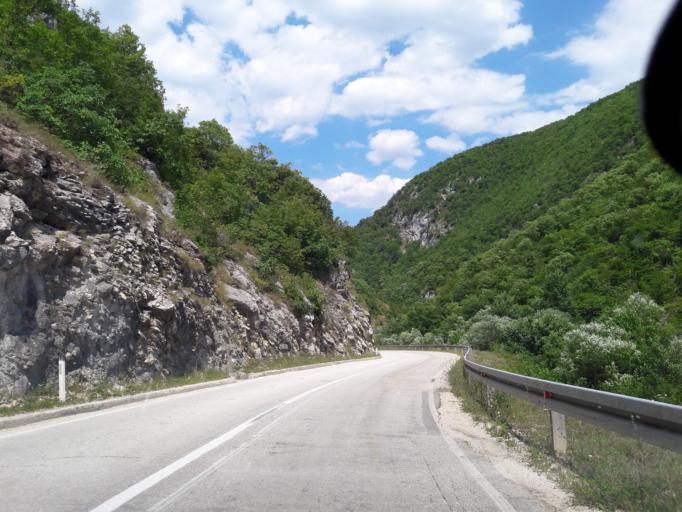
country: BA
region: Republika Srpska
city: Mrkonjic Grad
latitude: 44.4580
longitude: 17.1595
